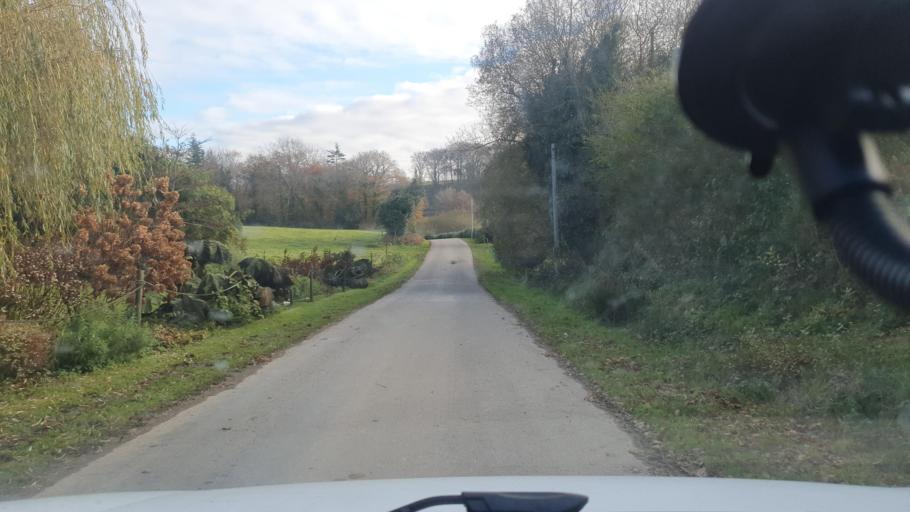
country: FR
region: Brittany
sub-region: Departement du Finistere
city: Landrevarzec
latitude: 48.1049
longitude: -4.0399
